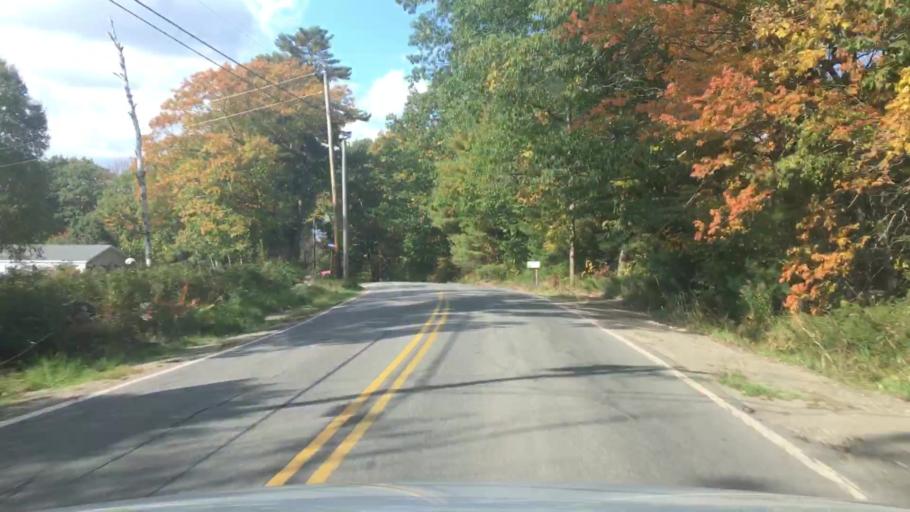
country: US
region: Maine
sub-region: Knox County
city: Union
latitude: 44.1735
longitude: -69.2532
